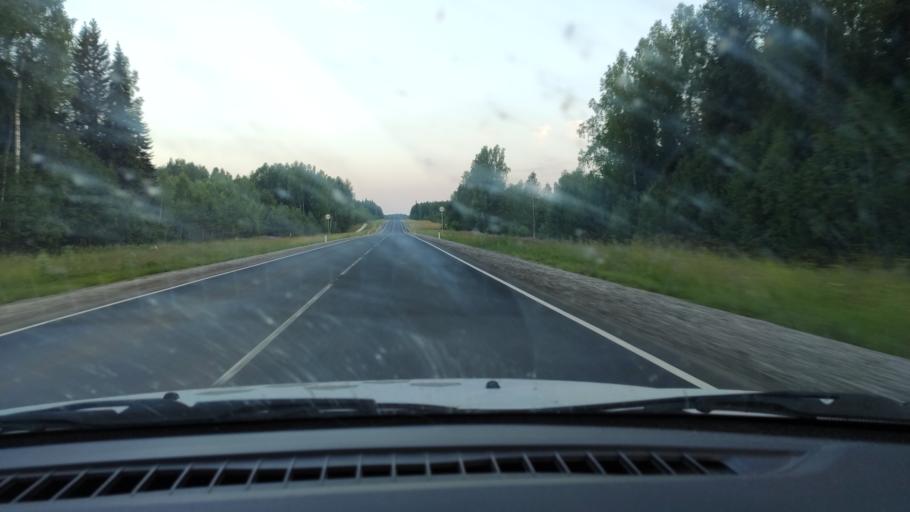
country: RU
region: Perm
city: Siva
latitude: 58.3951
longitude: 54.5202
